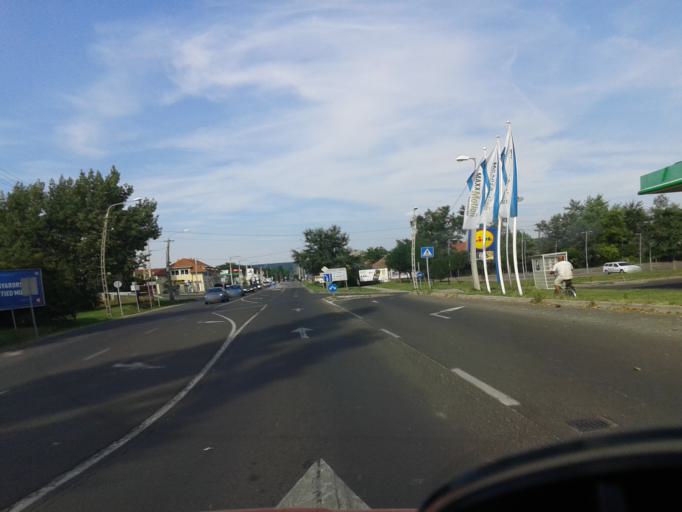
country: HU
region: Pest
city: Kistarcsa
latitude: 47.5495
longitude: 19.2662
